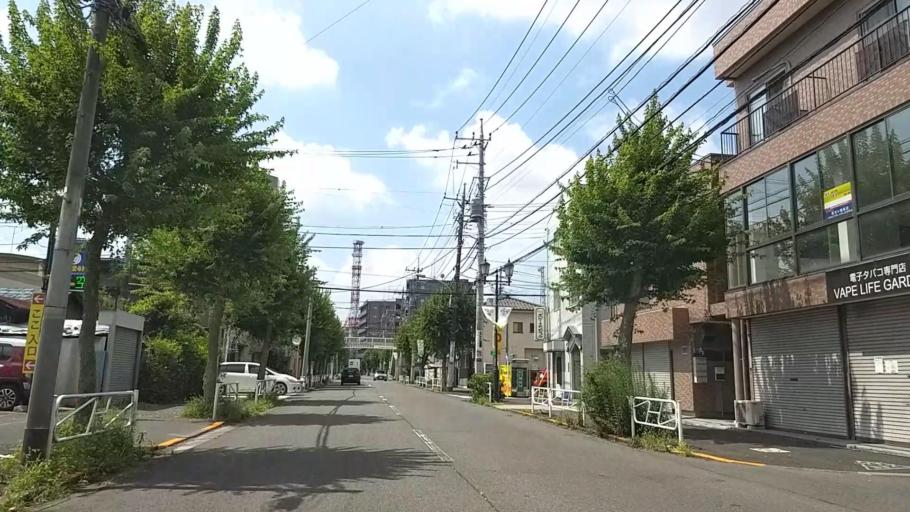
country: JP
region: Tokyo
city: Hachioji
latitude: 35.6587
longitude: 139.3456
